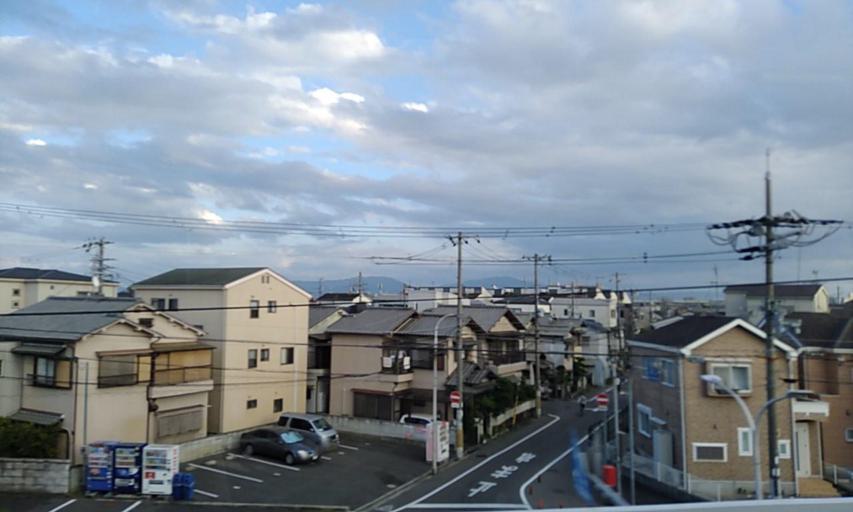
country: JP
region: Osaka
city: Matsubara
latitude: 34.5445
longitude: 135.5128
